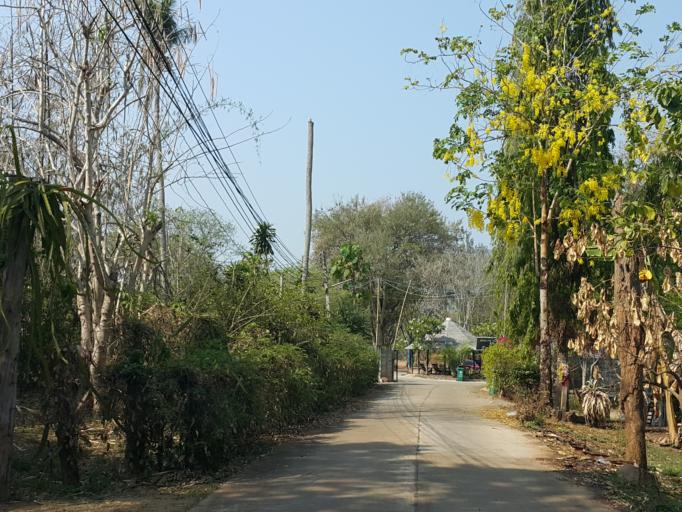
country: TH
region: Kanchanaburi
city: Sai Yok
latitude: 14.1145
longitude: 99.1362
